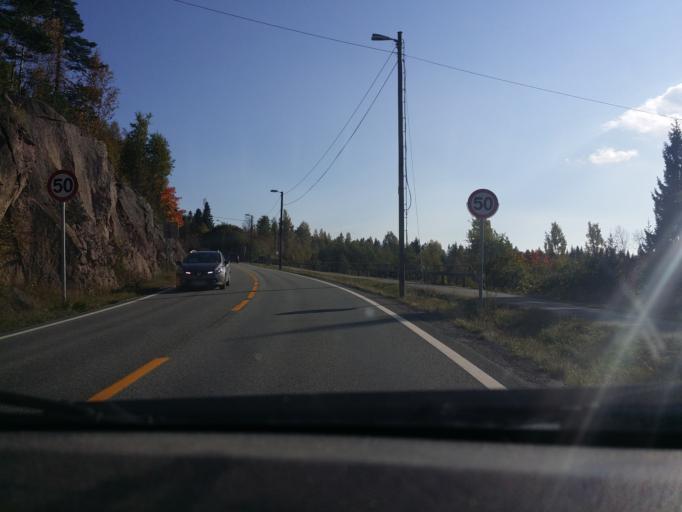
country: NO
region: Akershus
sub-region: Baerum
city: Skui
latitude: 59.9653
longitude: 10.3419
